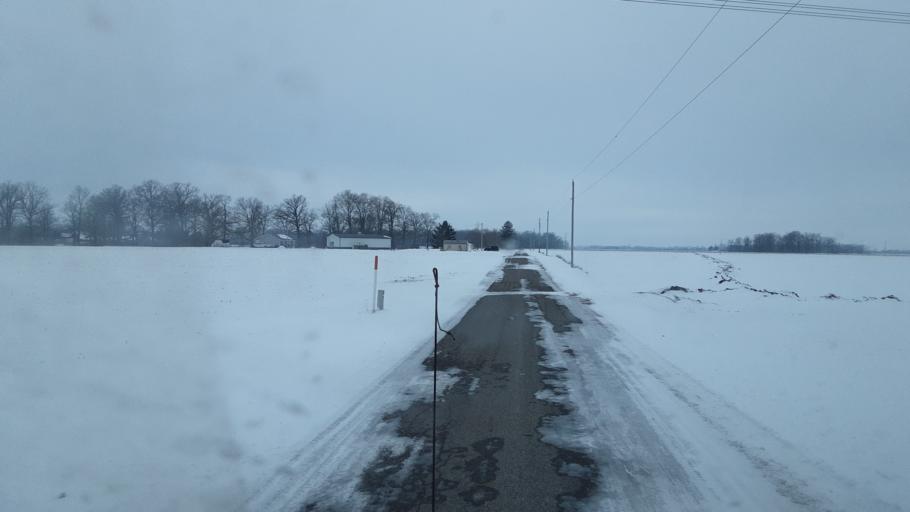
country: US
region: Ohio
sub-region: Union County
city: Marysville
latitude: 40.1266
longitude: -83.4171
